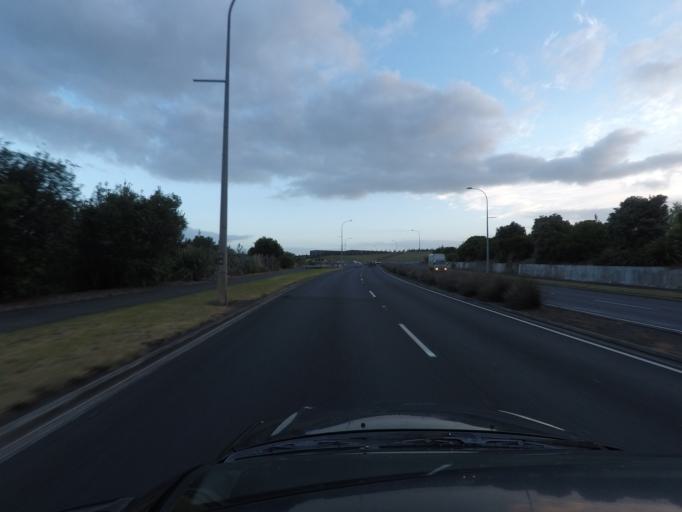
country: NZ
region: Auckland
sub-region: Auckland
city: Manukau City
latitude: -36.9471
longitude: 174.8603
